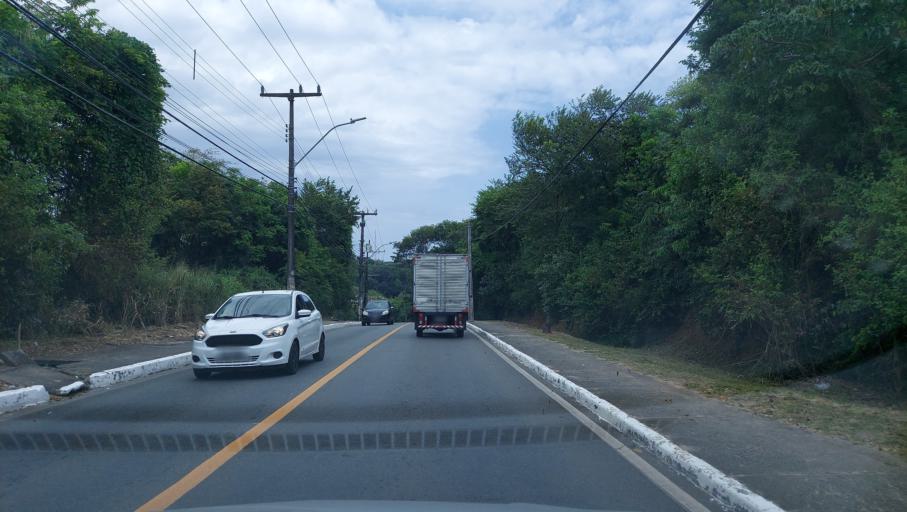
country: BR
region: Bahia
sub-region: Salvador
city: Salvador
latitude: -12.9667
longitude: -38.4432
